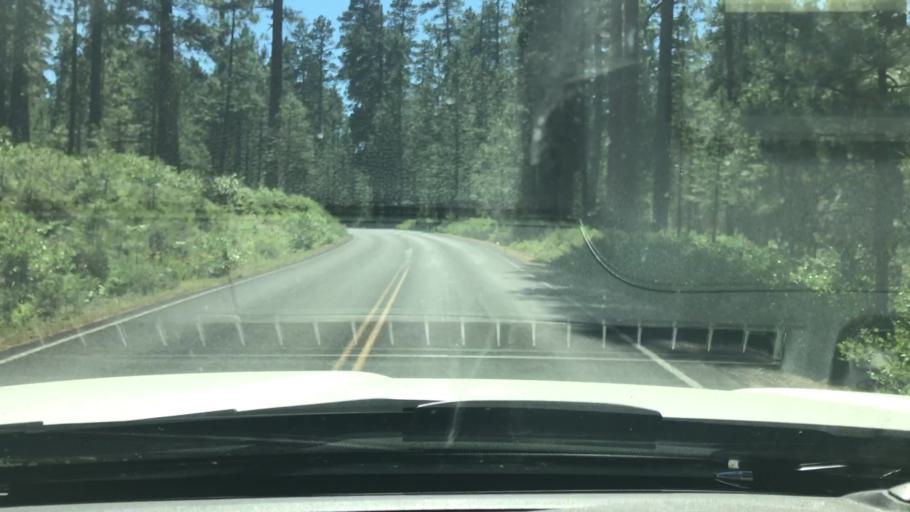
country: US
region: Oregon
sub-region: Deschutes County
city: Sisters
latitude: 44.4239
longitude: -121.6660
